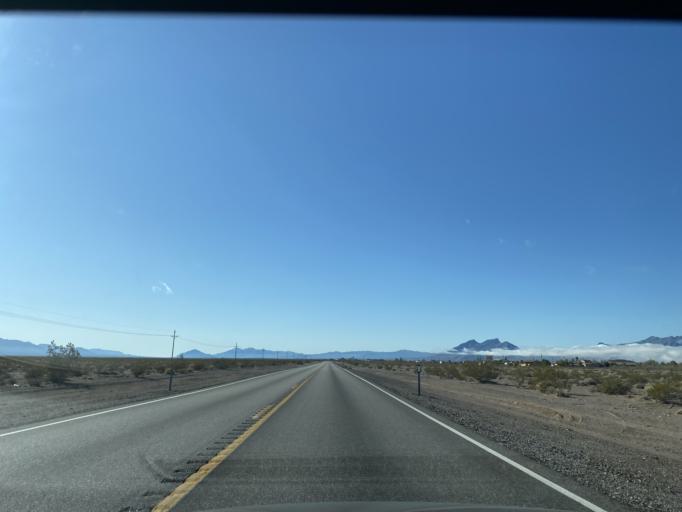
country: US
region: Nevada
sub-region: Nye County
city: Beatty
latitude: 36.5166
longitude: -116.4201
